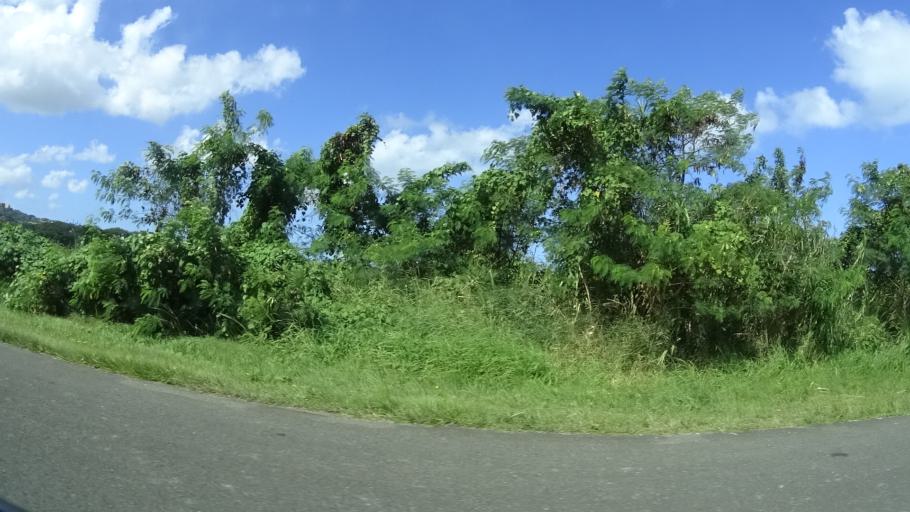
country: PR
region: Luquillo
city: Playa Fortuna
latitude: 18.3789
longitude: -65.7511
